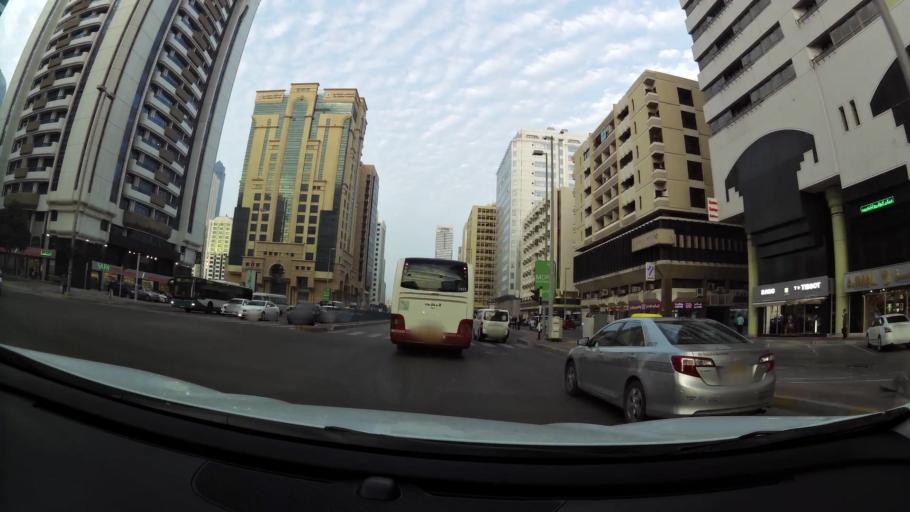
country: AE
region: Abu Dhabi
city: Abu Dhabi
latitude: 24.4777
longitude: 54.3532
